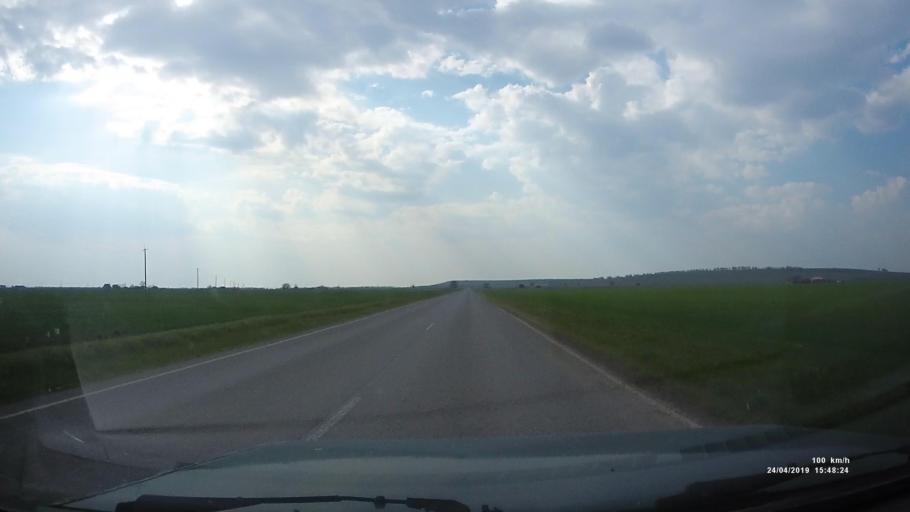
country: RU
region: Kalmykiya
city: Yashalta
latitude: 46.5984
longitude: 42.6768
